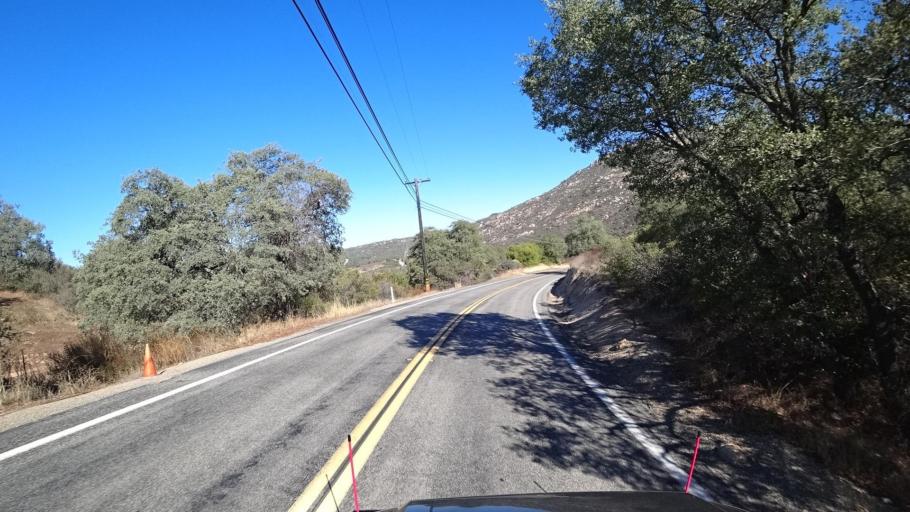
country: US
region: California
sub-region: San Diego County
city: Jamul
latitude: 32.7083
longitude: -116.7493
